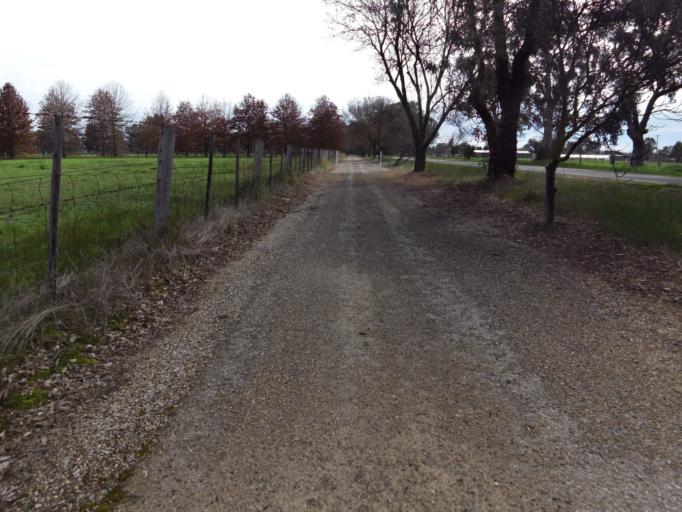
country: AU
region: Victoria
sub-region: Wangaratta
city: Wangaratta
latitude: -36.4344
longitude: 146.3578
